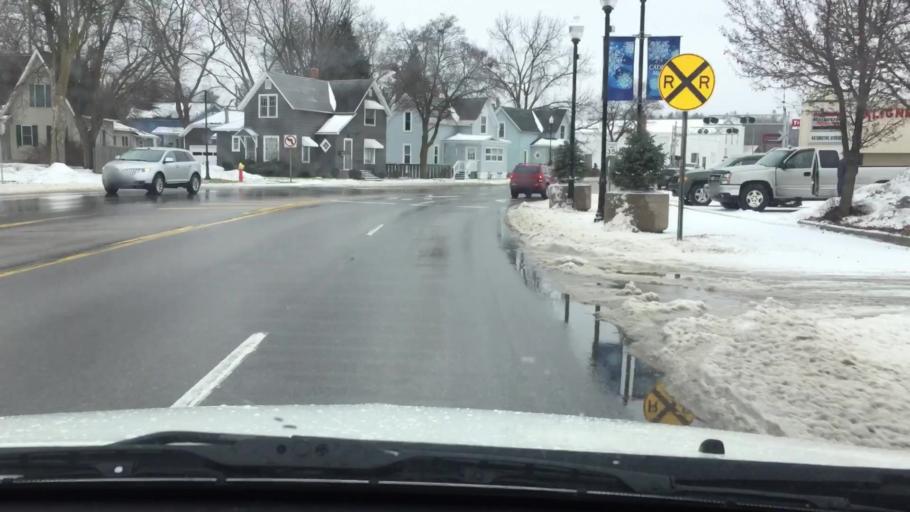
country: US
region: Michigan
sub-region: Wexford County
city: Cadillac
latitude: 44.2469
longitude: -85.3967
